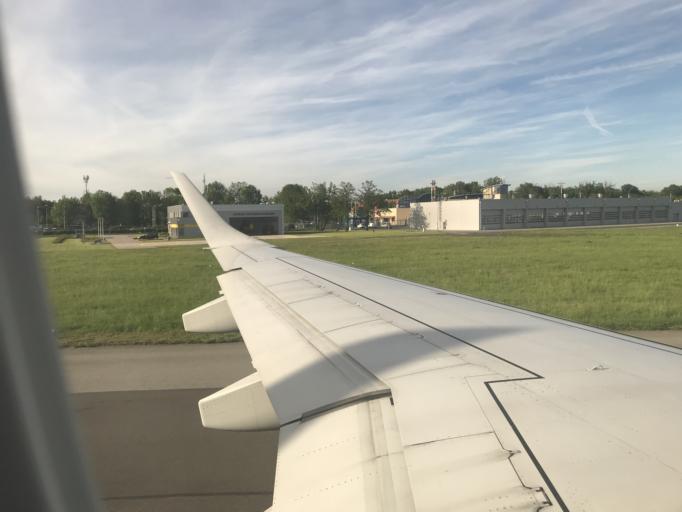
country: PL
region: Lower Silesian Voivodeship
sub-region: Powiat wroclawski
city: Smolec
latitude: 51.1027
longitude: 16.8972
